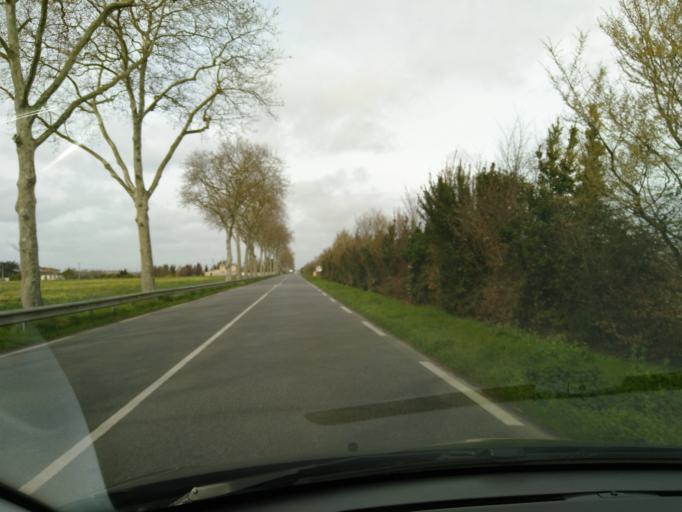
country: FR
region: Midi-Pyrenees
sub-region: Departement de la Haute-Garonne
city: Seilh
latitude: 43.7081
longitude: 1.3414
